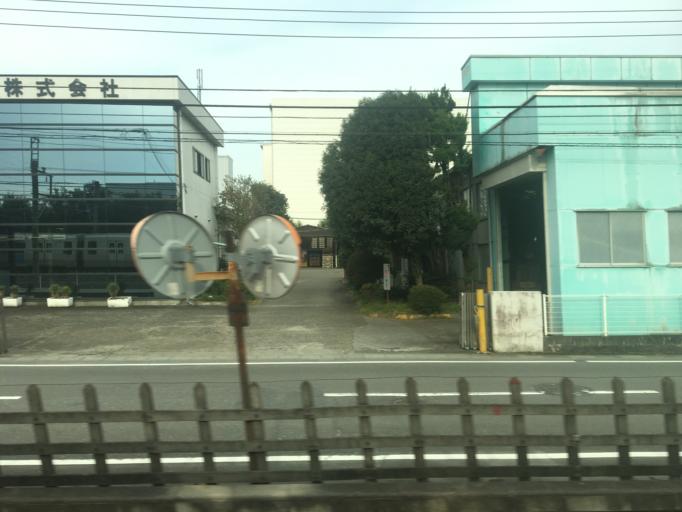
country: JP
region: Saitama
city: Sayama
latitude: 35.8806
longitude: 139.4420
